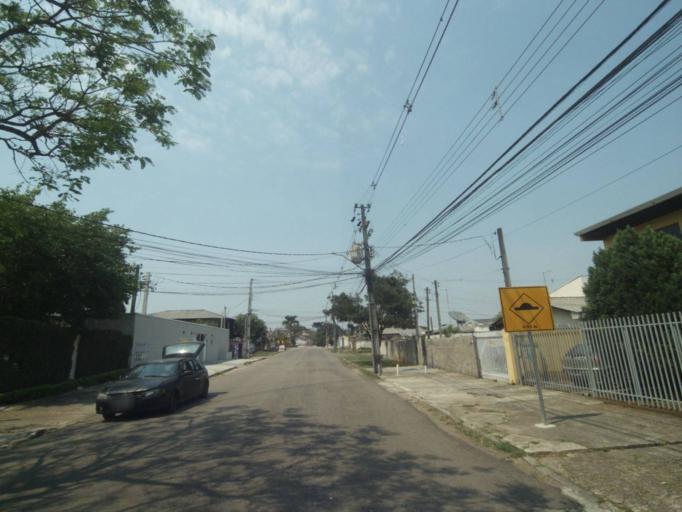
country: BR
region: Parana
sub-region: Sao Jose Dos Pinhais
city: Sao Jose dos Pinhais
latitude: -25.5407
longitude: -49.2465
